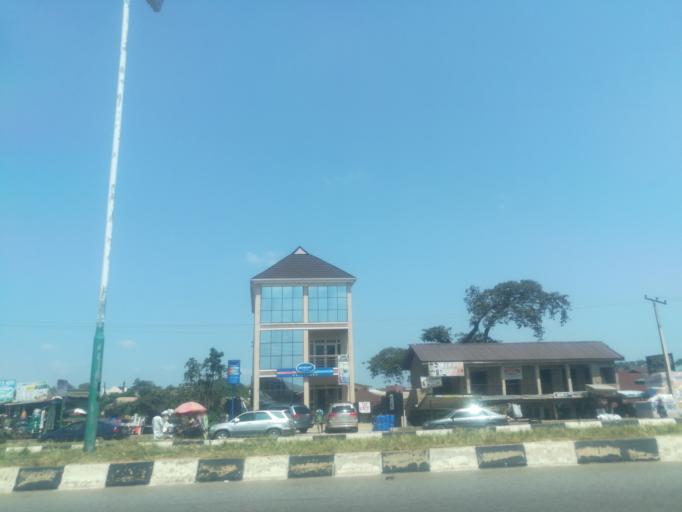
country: NG
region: Ogun
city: Abeokuta
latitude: 7.1559
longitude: 3.3446
